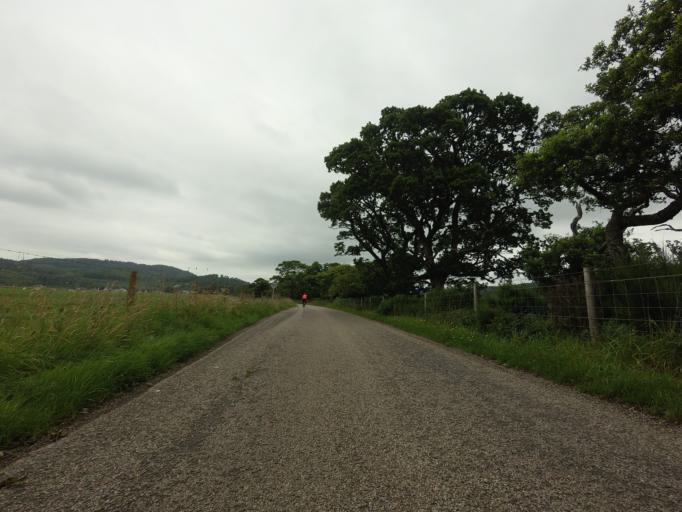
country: GB
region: Scotland
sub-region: Highland
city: Evanton
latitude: 57.9146
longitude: -4.3998
